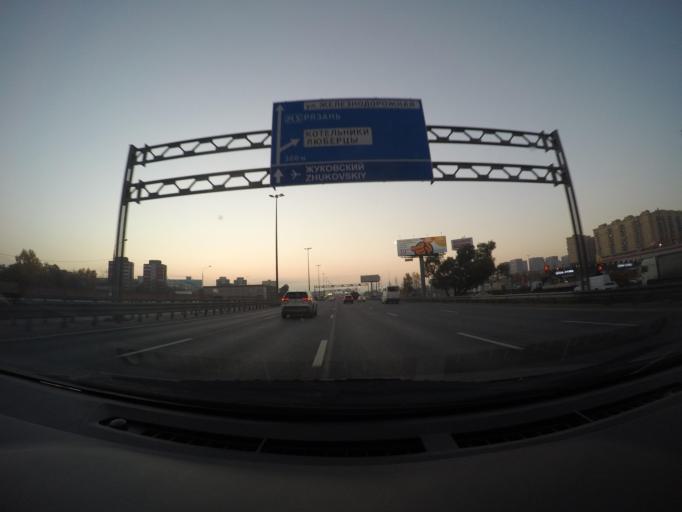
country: RU
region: Moskovskaya
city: Lyubertsy
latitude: 55.6692
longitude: 37.8712
